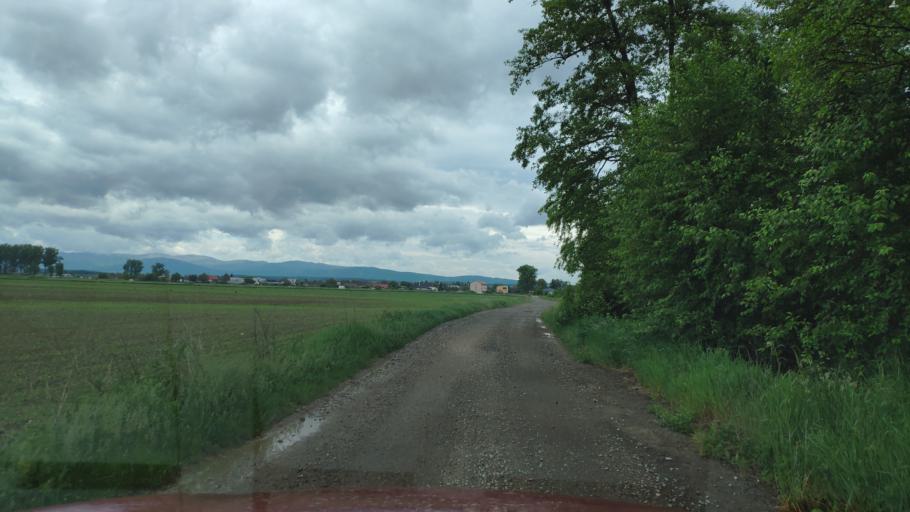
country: SK
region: Kosicky
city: Moldava nad Bodvou
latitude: 48.5641
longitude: 21.1210
